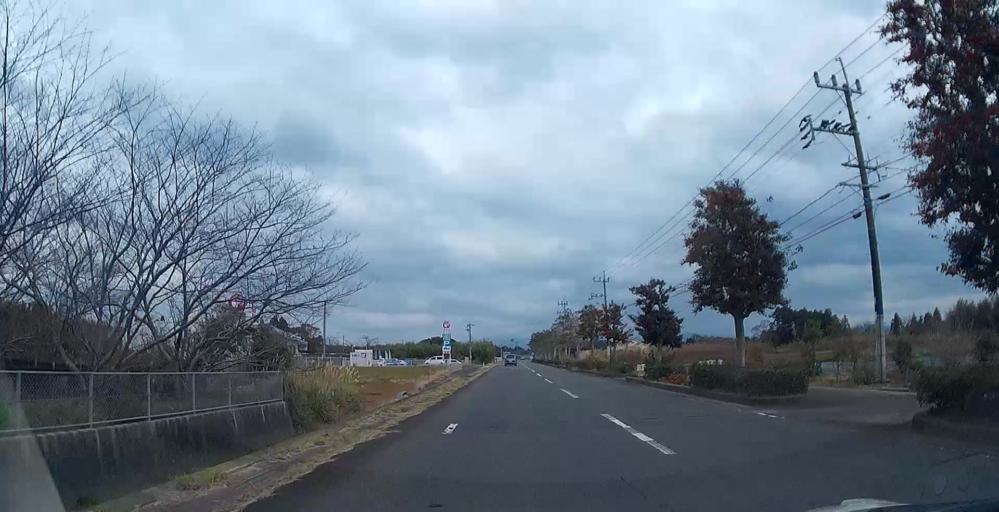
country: JP
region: Kagoshima
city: Akune
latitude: 32.0760
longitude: 130.2093
